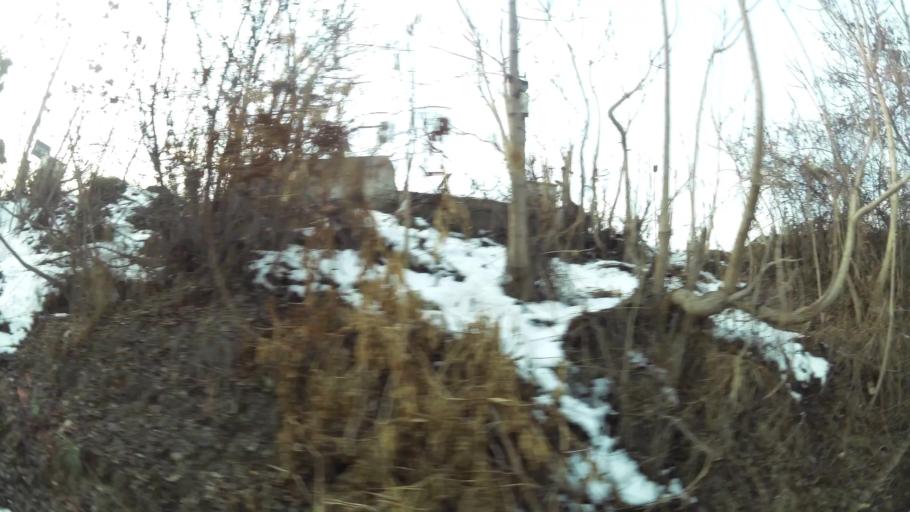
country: MK
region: Karpos
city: Skopje
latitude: 42.0129
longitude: 21.4076
